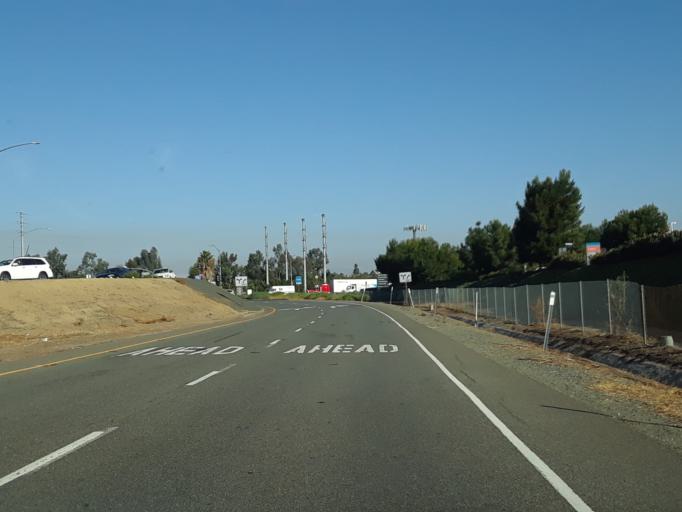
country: US
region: California
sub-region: Orange County
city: Irvine
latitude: 33.6575
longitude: -117.7757
